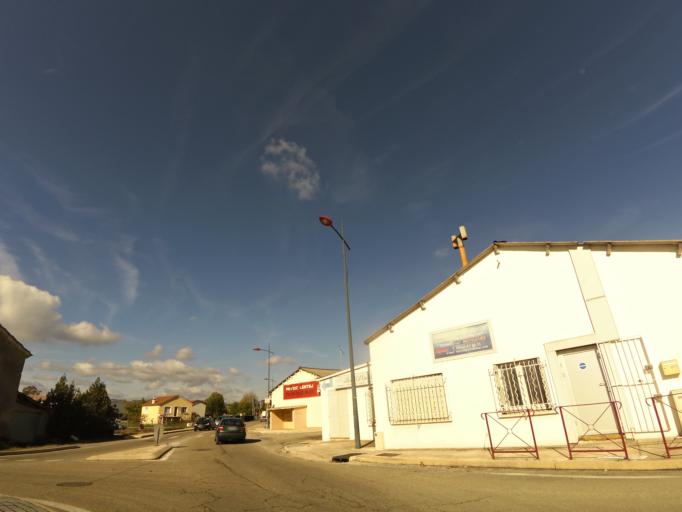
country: FR
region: Languedoc-Roussillon
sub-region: Departement du Gard
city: Saint-Christol-les-Ales
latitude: 44.0757
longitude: 4.0801
